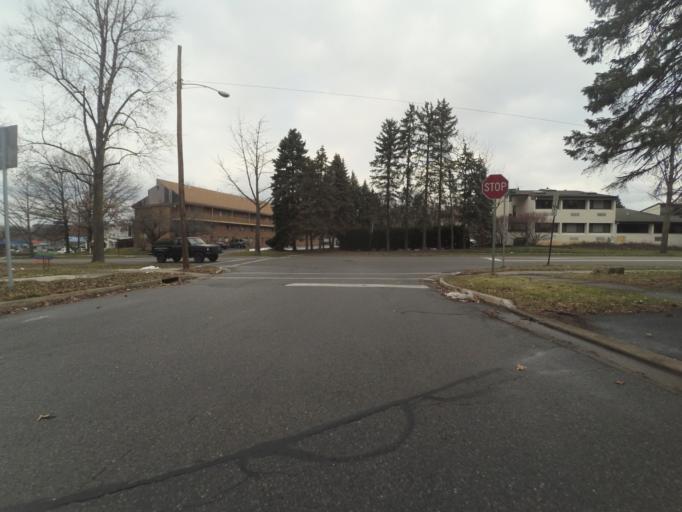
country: US
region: Pennsylvania
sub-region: Centre County
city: State College
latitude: 40.7979
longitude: -77.8463
